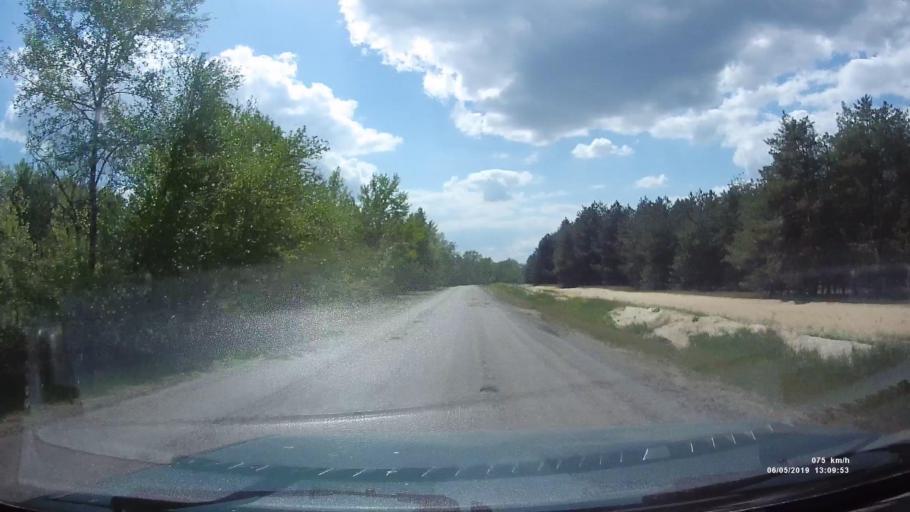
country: RU
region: Rostov
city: Ust'-Donetskiy
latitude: 47.7650
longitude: 40.9784
